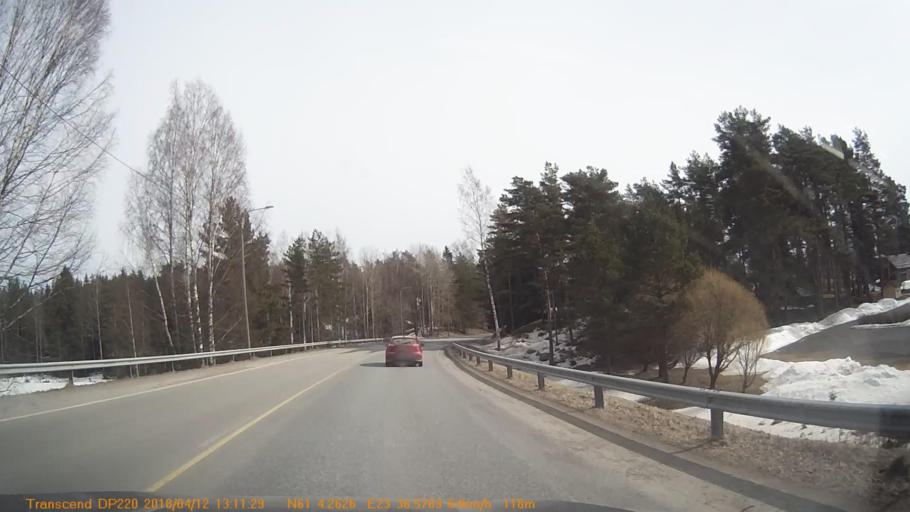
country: FI
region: Pirkanmaa
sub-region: Etelae-Pirkanmaa
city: Urjala
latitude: 61.0709
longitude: 23.6110
